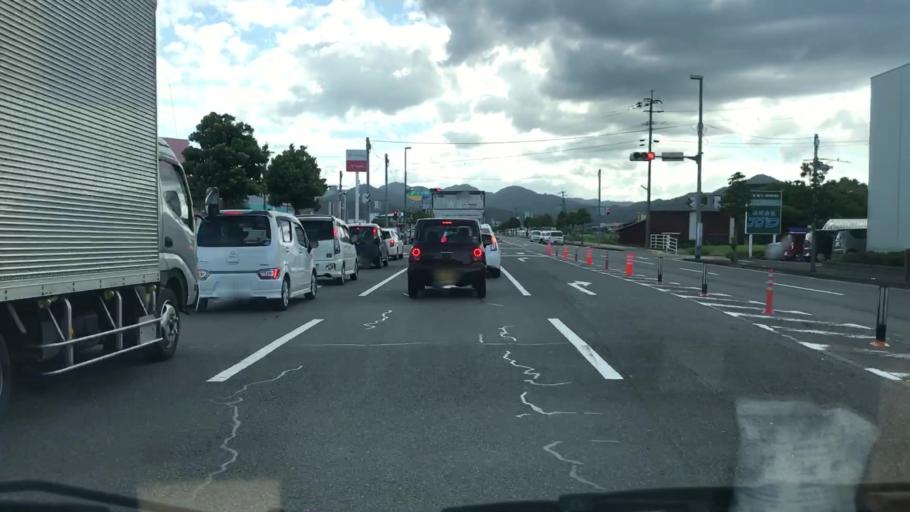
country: JP
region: Saga Prefecture
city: Kashima
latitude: 33.1263
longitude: 130.1018
